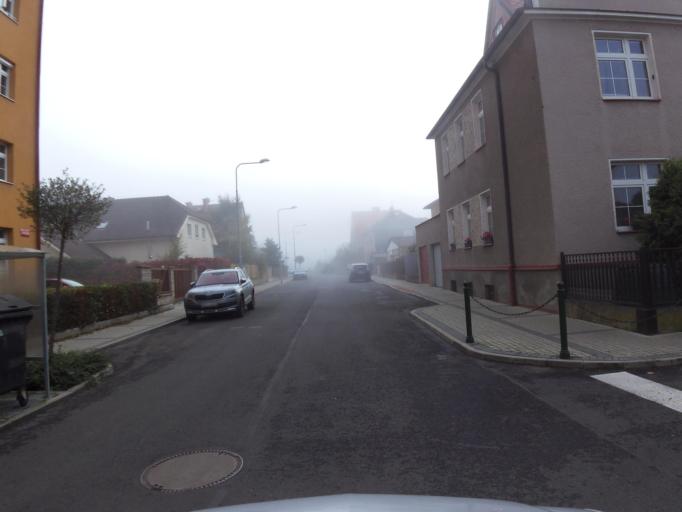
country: CZ
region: Ustecky
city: Zatec
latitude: 50.3202
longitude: 13.5526
